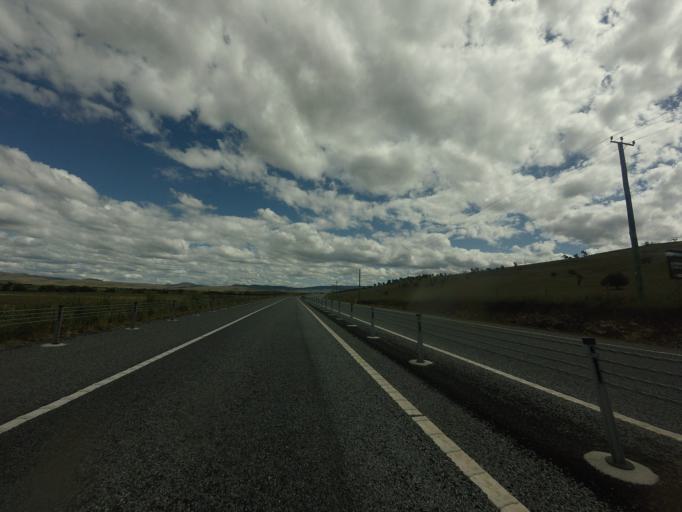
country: AU
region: Tasmania
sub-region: Northern Midlands
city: Evandale
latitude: -42.1172
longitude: 147.4399
